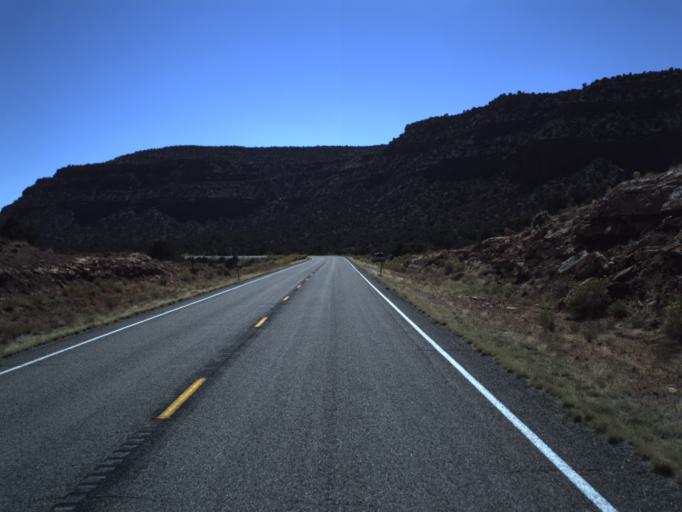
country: US
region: Utah
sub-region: San Juan County
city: Blanding
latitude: 37.6395
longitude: -110.1088
